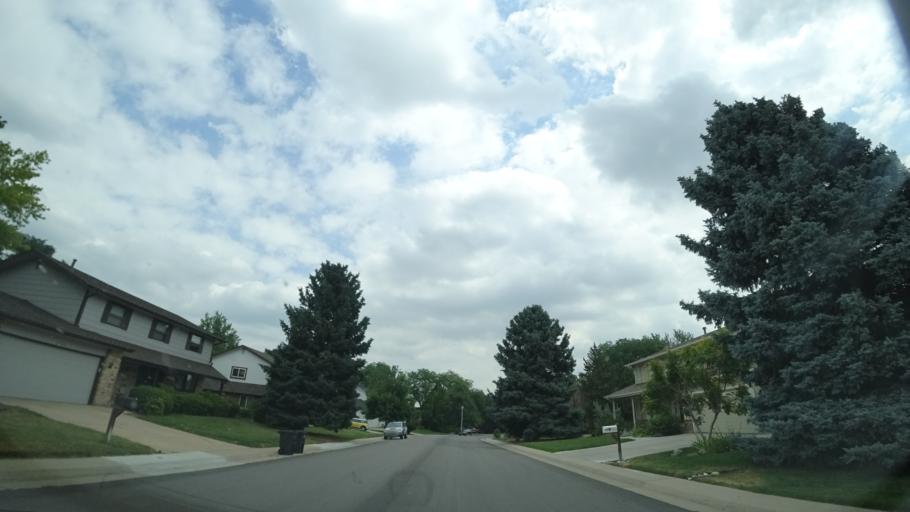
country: US
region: Colorado
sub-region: Jefferson County
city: West Pleasant View
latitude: 39.7198
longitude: -105.1570
